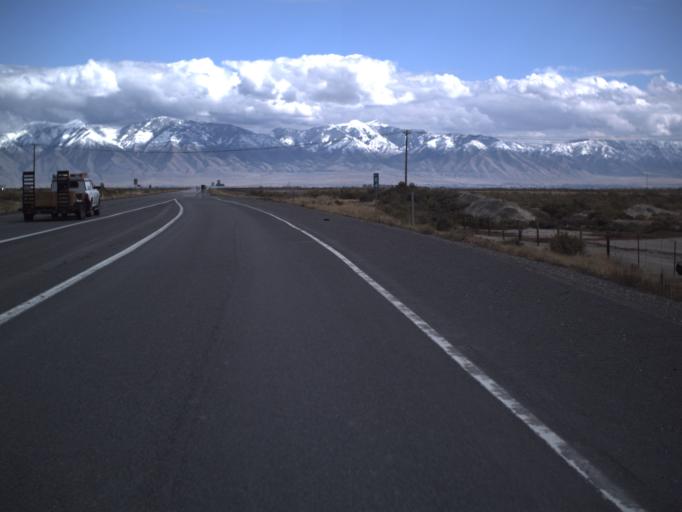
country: US
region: Utah
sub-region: Tooele County
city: Grantsville
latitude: 40.7061
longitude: -112.5209
